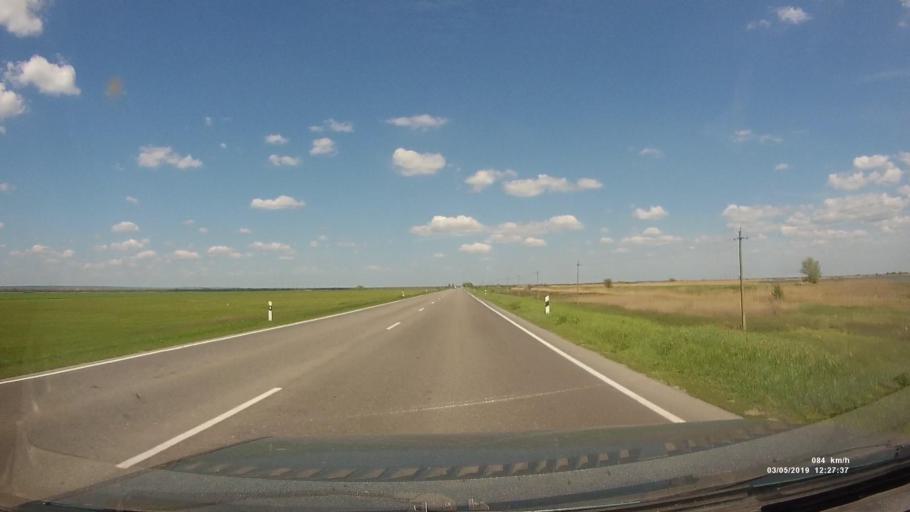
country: RU
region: Rostov
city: Semikarakorsk
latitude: 47.4615
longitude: 40.7221
